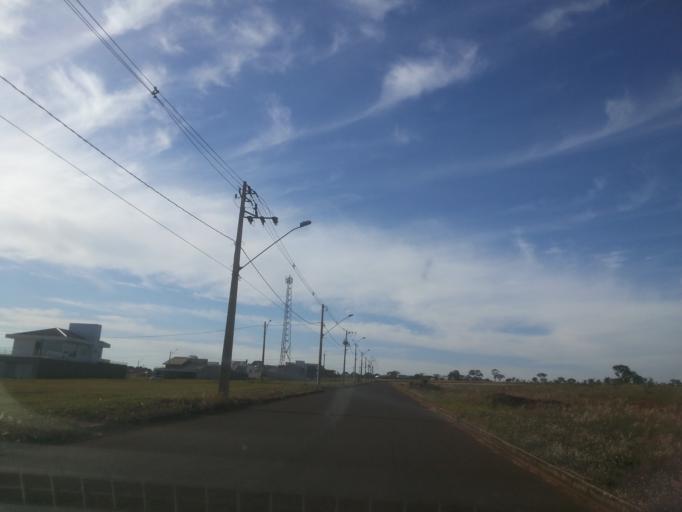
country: BR
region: Minas Gerais
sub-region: Ituiutaba
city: Ituiutaba
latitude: -19.0028
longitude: -49.4638
